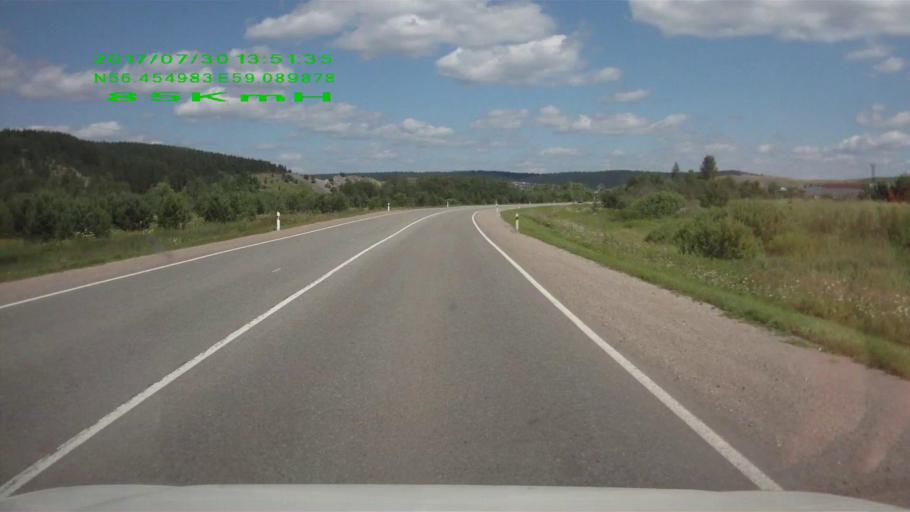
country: RU
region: Sverdlovsk
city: Mikhaylovsk
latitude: 56.4552
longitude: 59.0905
